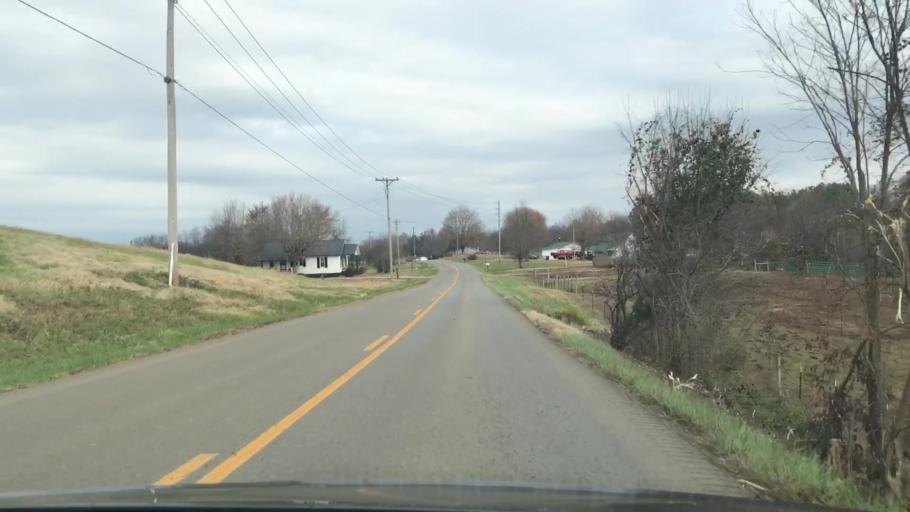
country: US
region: Kentucky
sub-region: Metcalfe County
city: Edmonton
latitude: 36.8865
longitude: -85.6647
